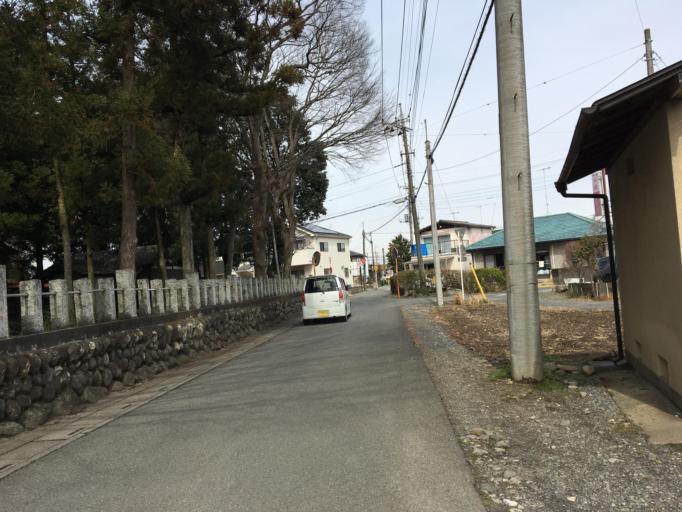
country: JP
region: Saitama
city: Yorii
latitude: 36.1279
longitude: 139.2207
